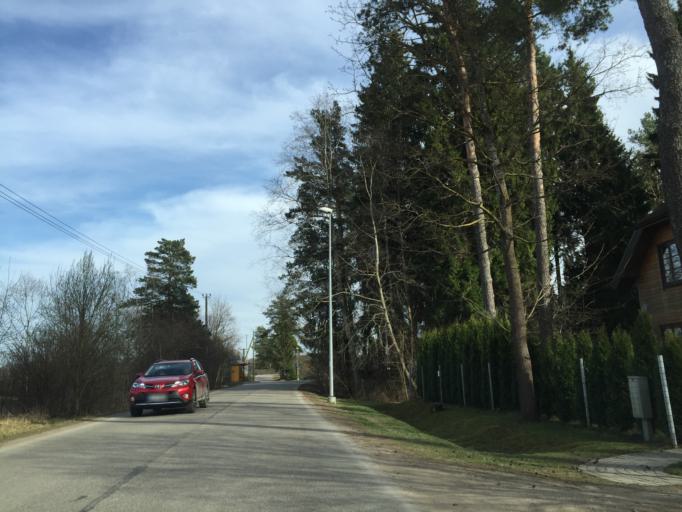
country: LV
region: Ogre
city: Ogre
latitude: 56.8103
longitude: 24.6320
